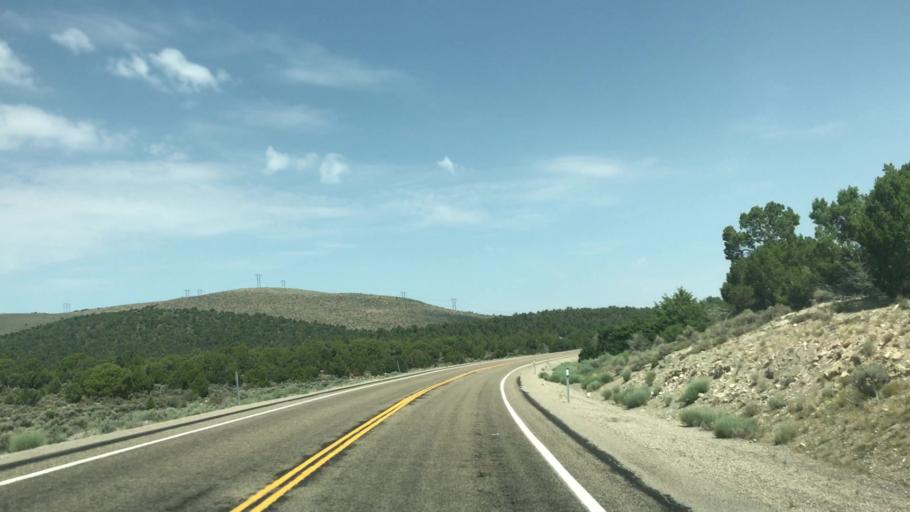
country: US
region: Nevada
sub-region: White Pine County
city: Ely
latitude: 39.3929
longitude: -115.0823
